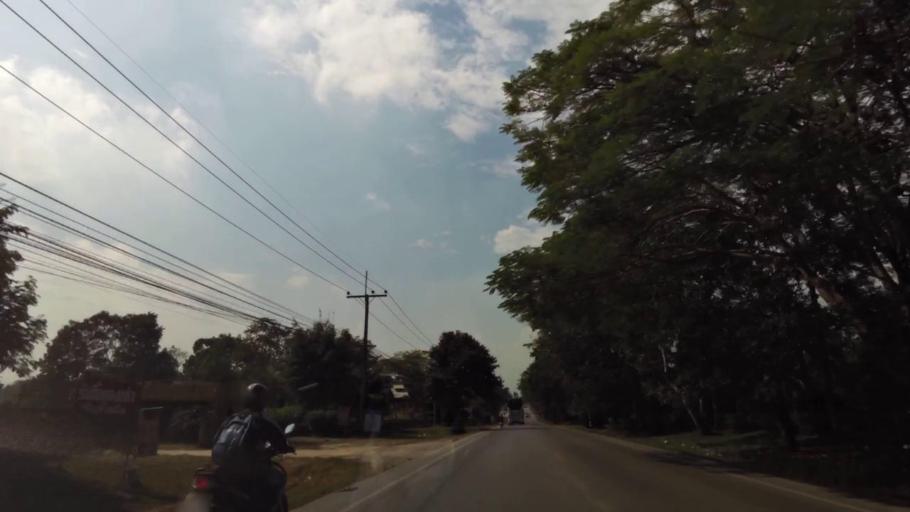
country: TH
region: Chiang Rai
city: Mae Lao
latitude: 19.8557
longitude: 99.7543
